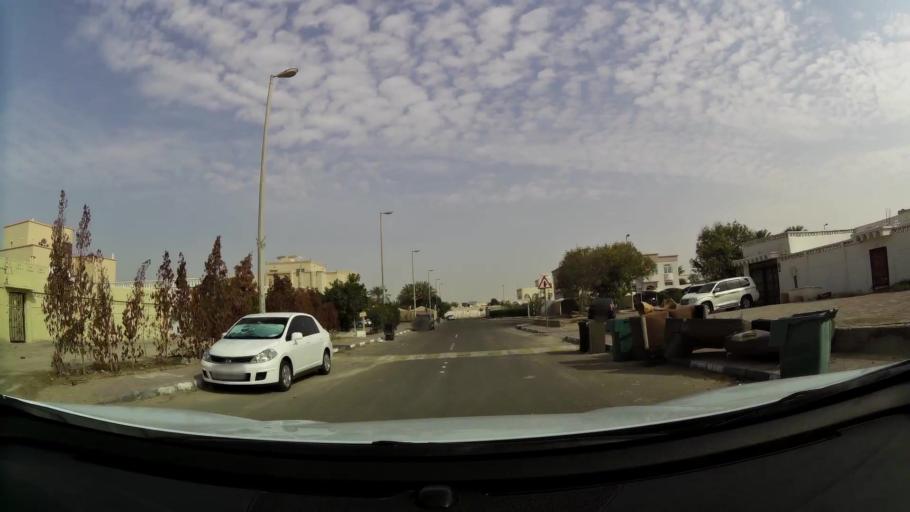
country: AE
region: Abu Dhabi
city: Abu Dhabi
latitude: 24.2610
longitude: 54.7008
